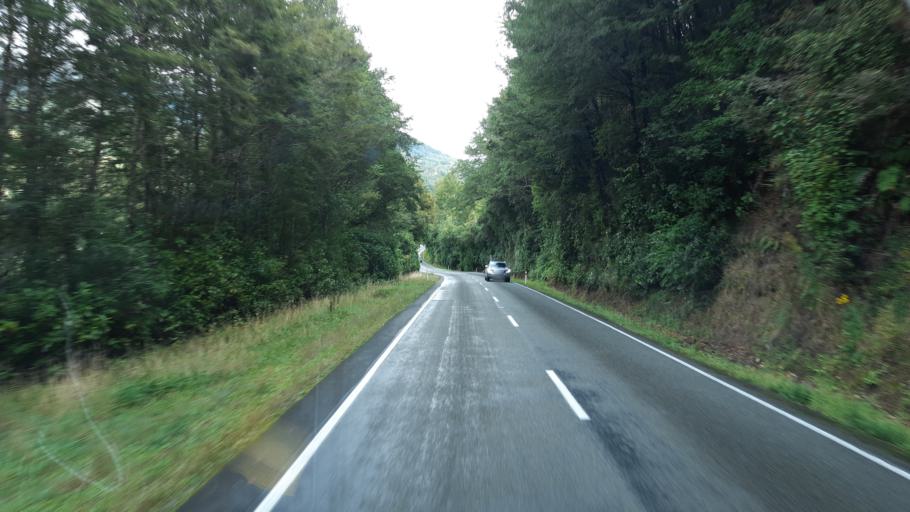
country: NZ
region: West Coast
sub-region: Buller District
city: Westport
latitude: -41.8117
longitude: 172.2293
